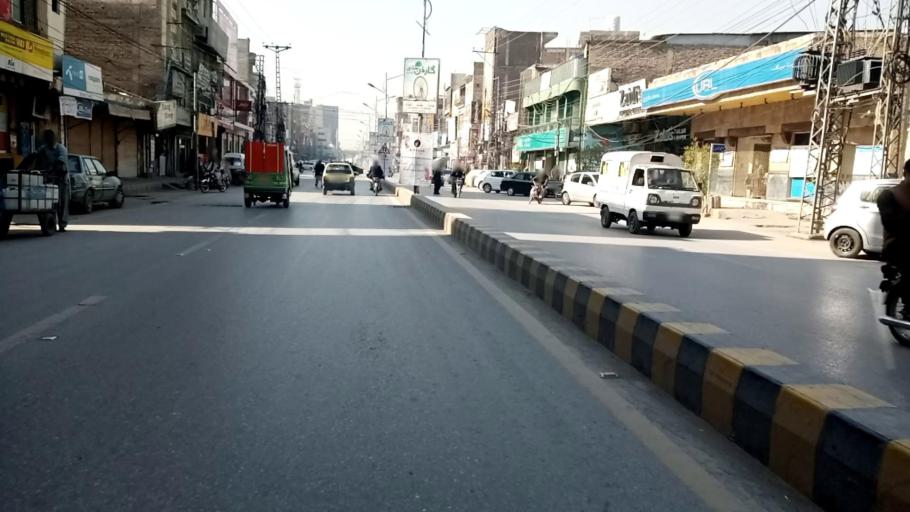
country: PK
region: Khyber Pakhtunkhwa
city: Peshawar
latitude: 33.9993
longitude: 71.5409
